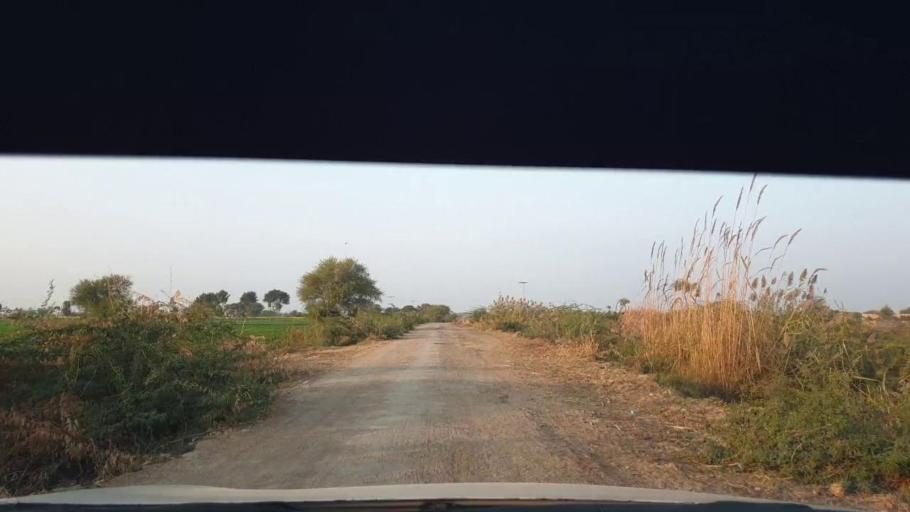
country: PK
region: Sindh
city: Berani
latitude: 25.7522
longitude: 68.9817
